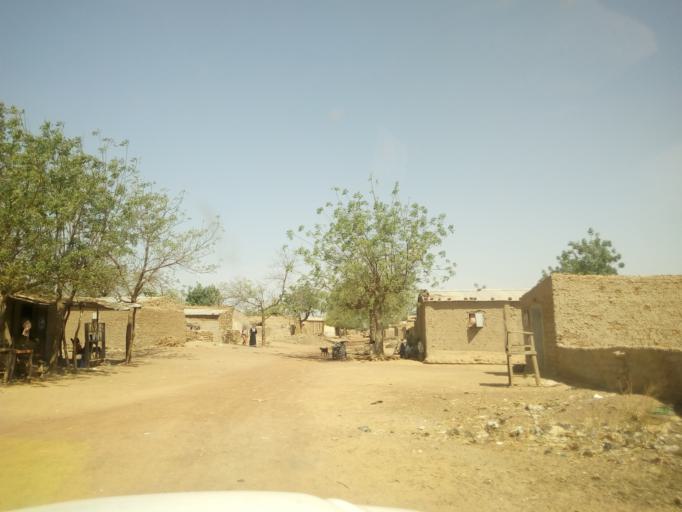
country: ML
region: Koulikoro
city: Koulikoro
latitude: 12.6483
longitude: -7.7100
